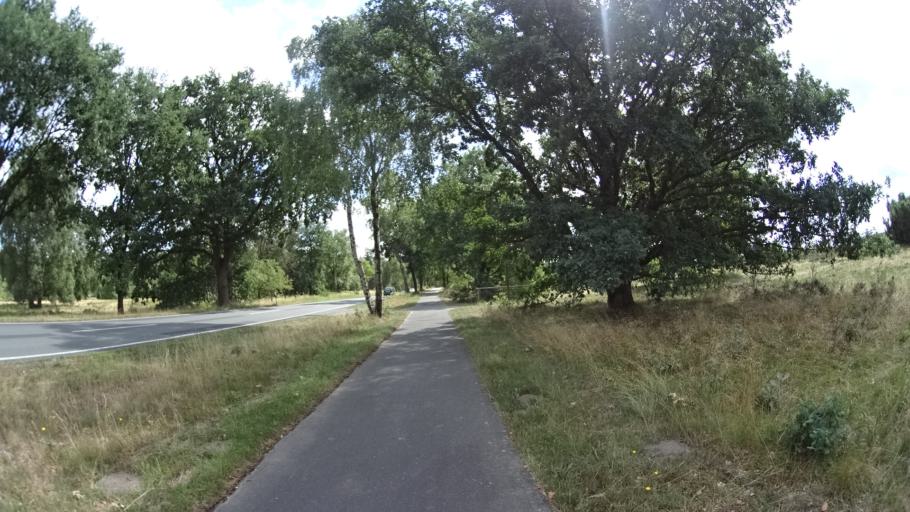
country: DE
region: Lower Saxony
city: Undeloh
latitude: 53.2141
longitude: 9.9489
